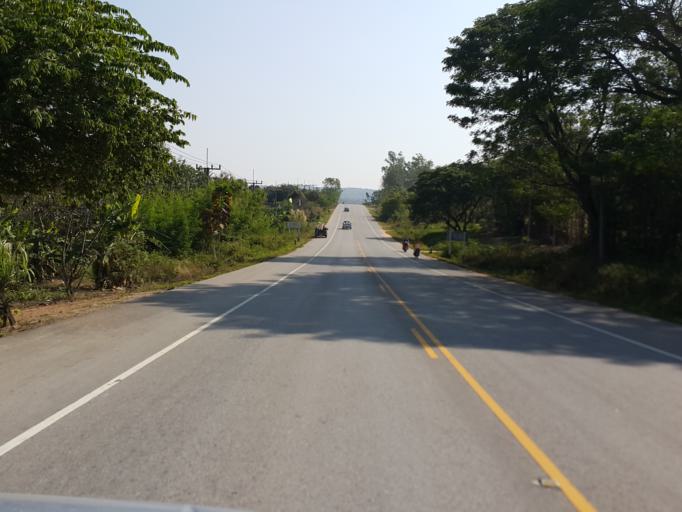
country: TH
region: Lampang
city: Wang Nuea
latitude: 18.9969
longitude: 99.6134
